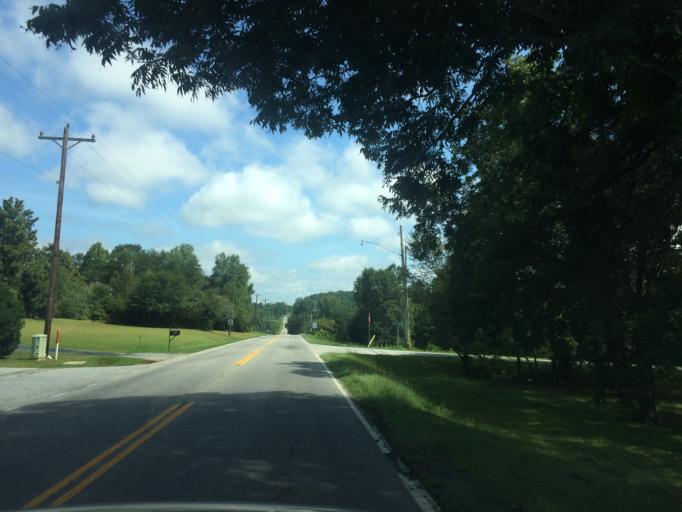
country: US
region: South Carolina
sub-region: Spartanburg County
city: Lyman
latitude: 34.9689
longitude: -82.1206
